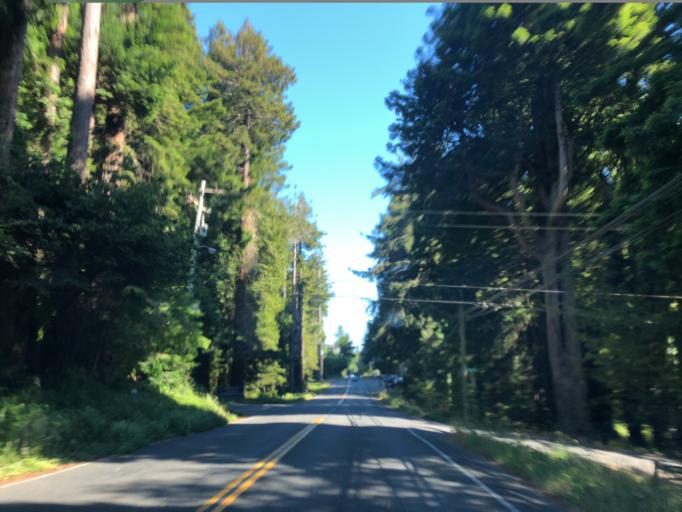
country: US
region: California
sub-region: Humboldt County
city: Westhaven-Moonstone
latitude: 41.0696
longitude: -124.1434
